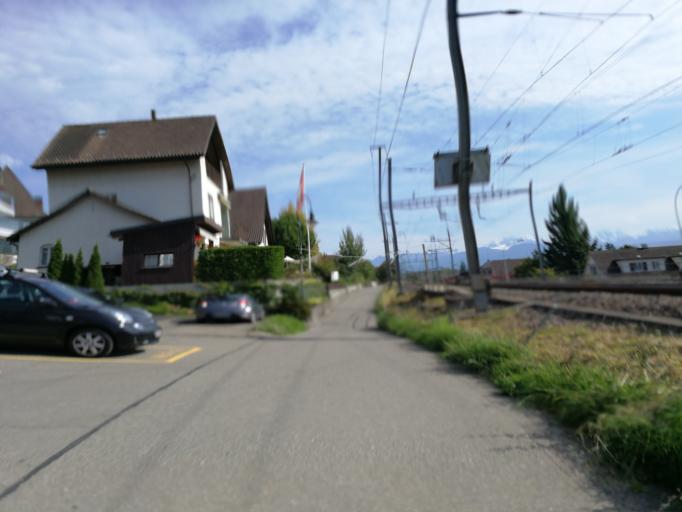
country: CH
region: Zurich
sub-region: Bezirk Meilen
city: Meilen
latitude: 47.2685
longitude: 8.6487
